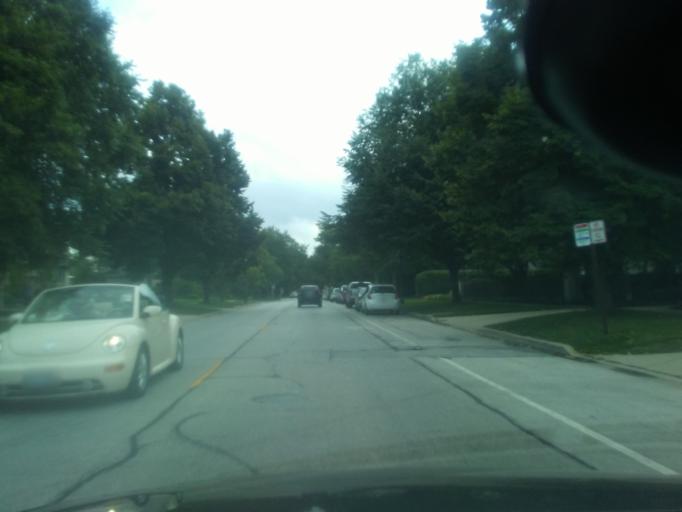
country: US
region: Illinois
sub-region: Cook County
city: Evanston
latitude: 42.0307
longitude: -87.6707
